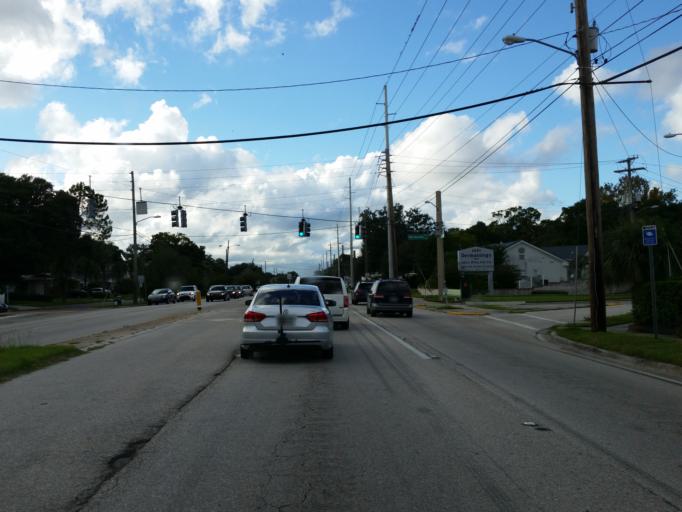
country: US
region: Florida
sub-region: Hillsborough County
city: Town 'n' Country
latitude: 27.9863
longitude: -82.5711
